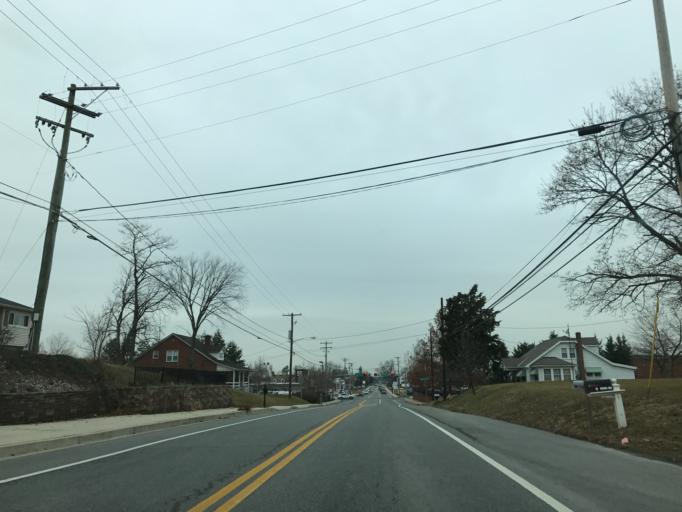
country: US
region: Maryland
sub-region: Carroll County
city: Taneytown
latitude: 39.6496
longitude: -77.1578
